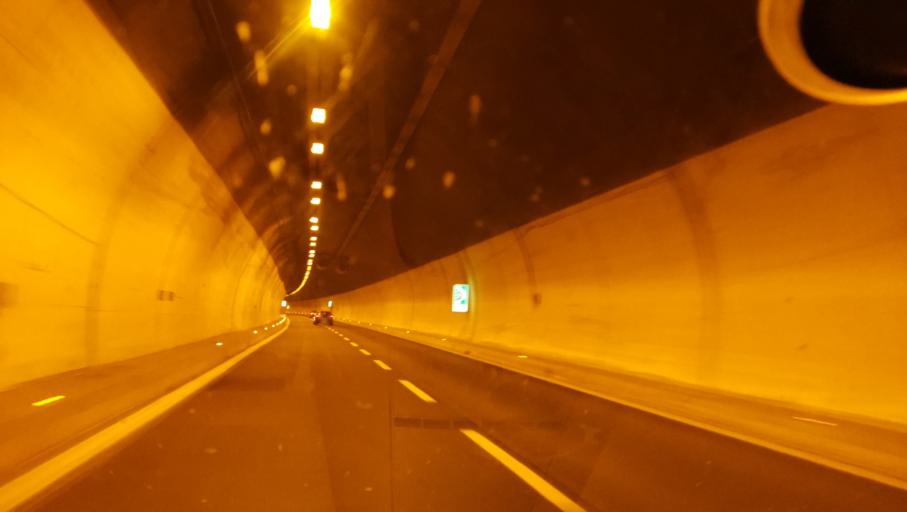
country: IT
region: Piedmont
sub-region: Provincia di Torino
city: Mattie
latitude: 45.1290
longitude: 7.1114
